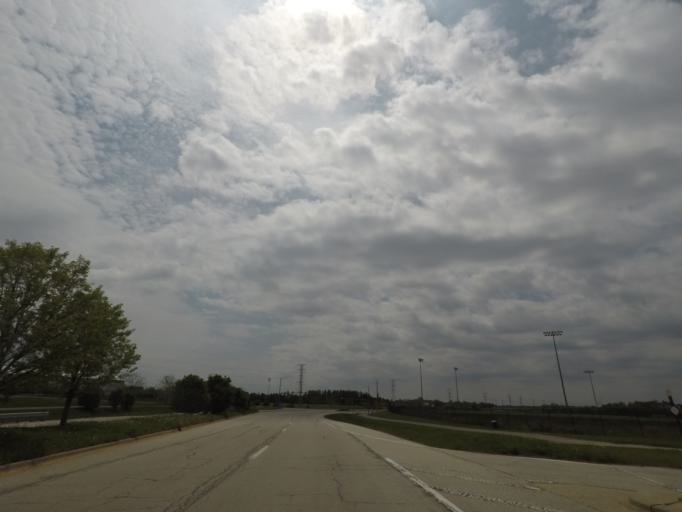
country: US
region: Illinois
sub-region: Winnebago County
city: Cherry Valley
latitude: 42.3233
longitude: -88.9495
